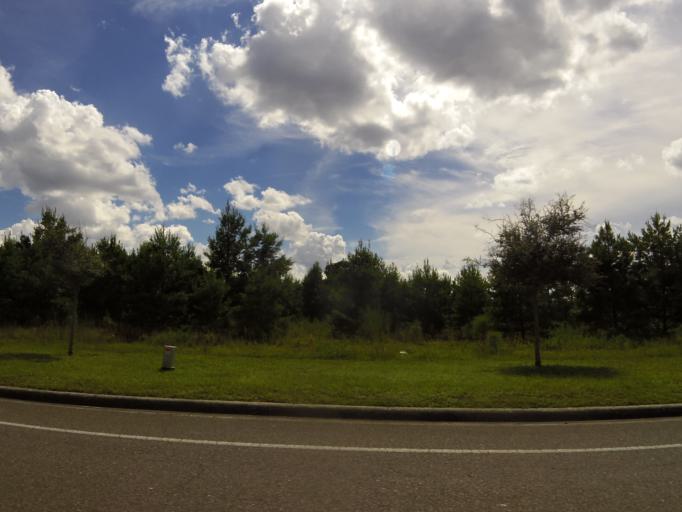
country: US
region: Florida
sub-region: Duval County
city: Jacksonville
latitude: 30.4285
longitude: -81.6368
